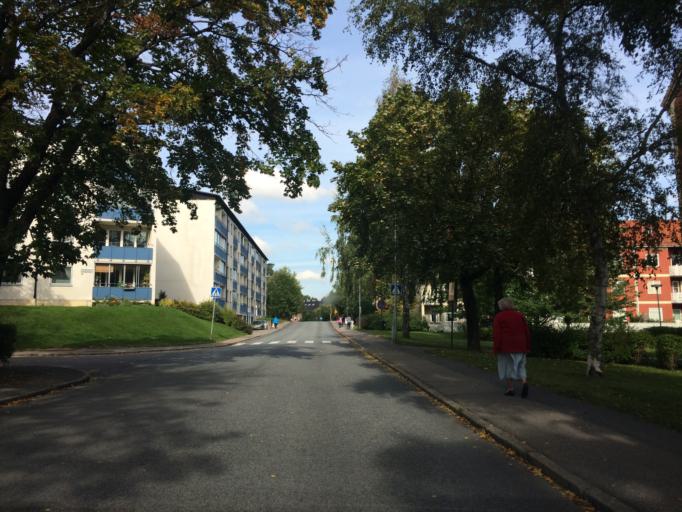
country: SE
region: Stockholm
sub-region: Sollentuna Kommun
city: Sollentuna
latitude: 59.4459
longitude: 17.9349
